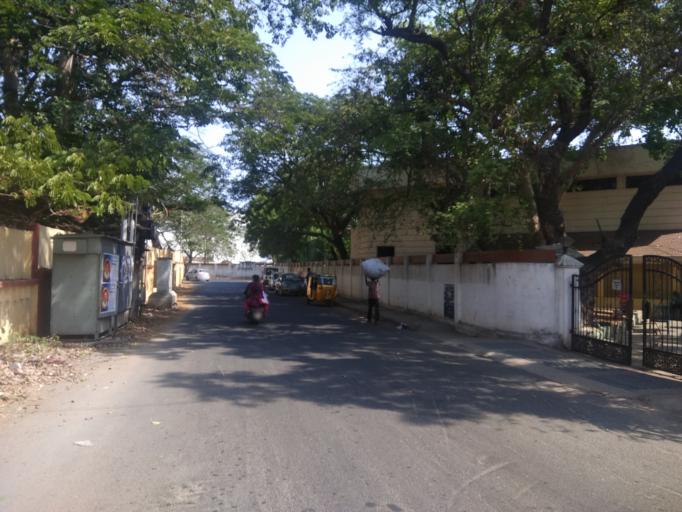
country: IN
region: Tamil Nadu
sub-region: Kancheepuram
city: Alandur
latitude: 13.0097
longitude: 80.2155
